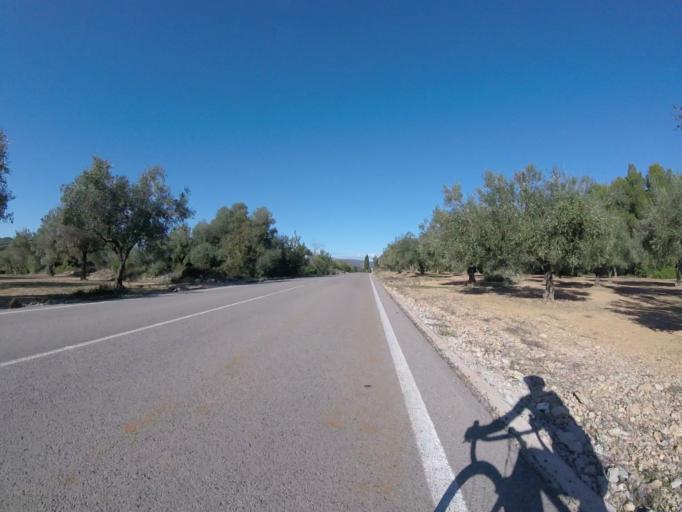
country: ES
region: Valencia
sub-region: Provincia de Castello
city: Cervera del Maestre
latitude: 40.4755
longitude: 0.2264
